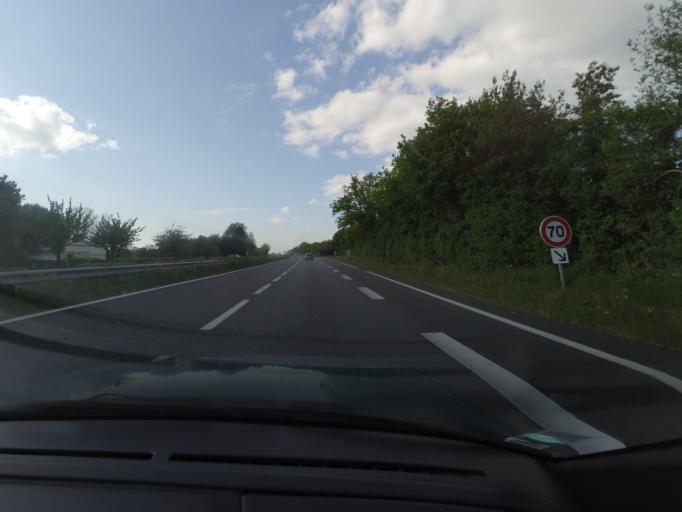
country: FR
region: Pays de la Loire
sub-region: Departement de la Vendee
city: Belleville-sur-Vie
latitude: 46.7805
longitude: -1.4200
